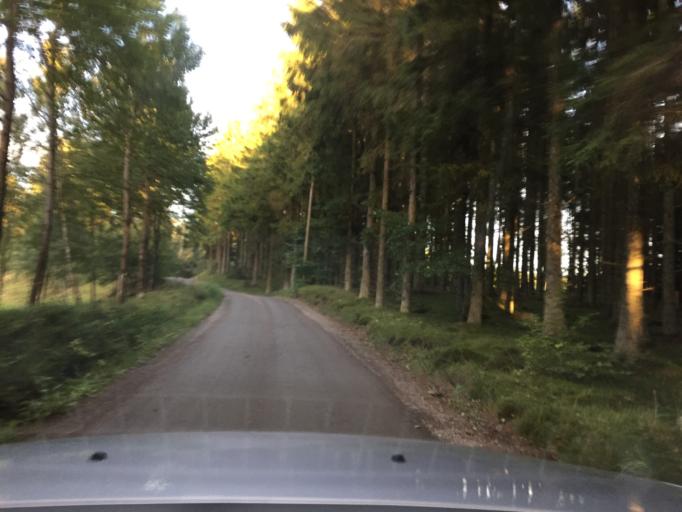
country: SE
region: Skane
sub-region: Hassleholms Kommun
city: Tormestorp
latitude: 56.0366
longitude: 13.7814
